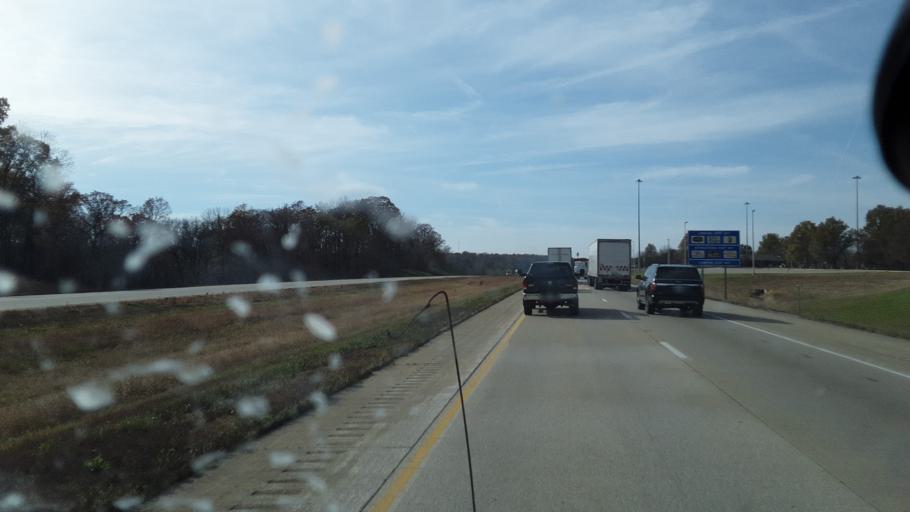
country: US
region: Illinois
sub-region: Clark County
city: Marshall
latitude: 39.4217
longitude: -87.6571
